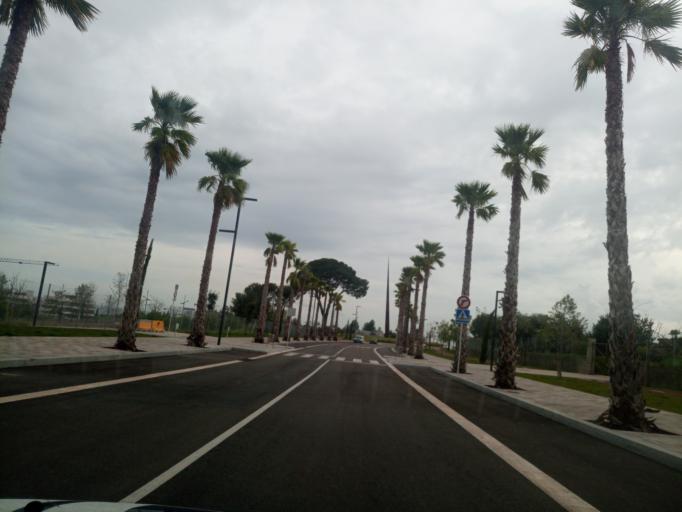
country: ES
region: Catalonia
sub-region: Provincia de Barcelona
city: Sitges
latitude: 41.2429
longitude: 1.7997
